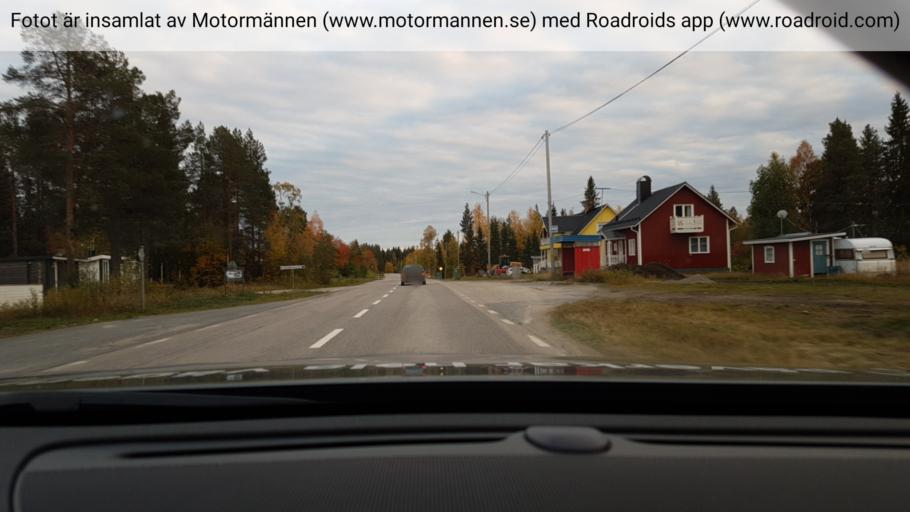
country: SE
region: Norrbotten
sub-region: Jokkmokks Kommun
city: Jokkmokk
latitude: 66.1549
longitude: 19.9810
